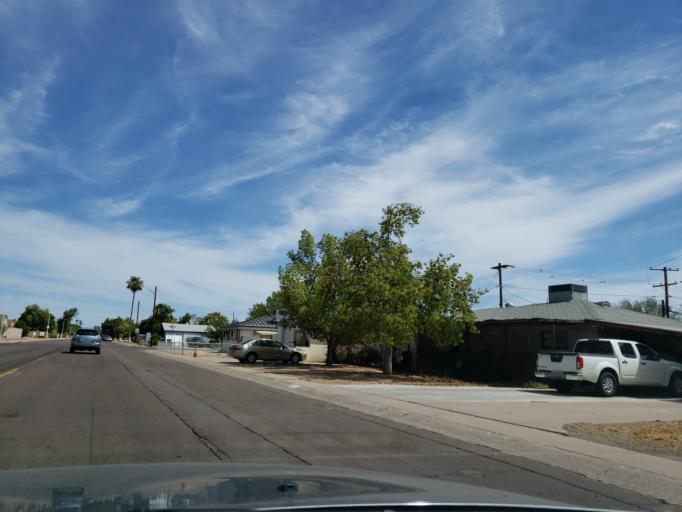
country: US
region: Arizona
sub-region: Maricopa County
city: Glendale
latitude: 33.5560
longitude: -112.1256
